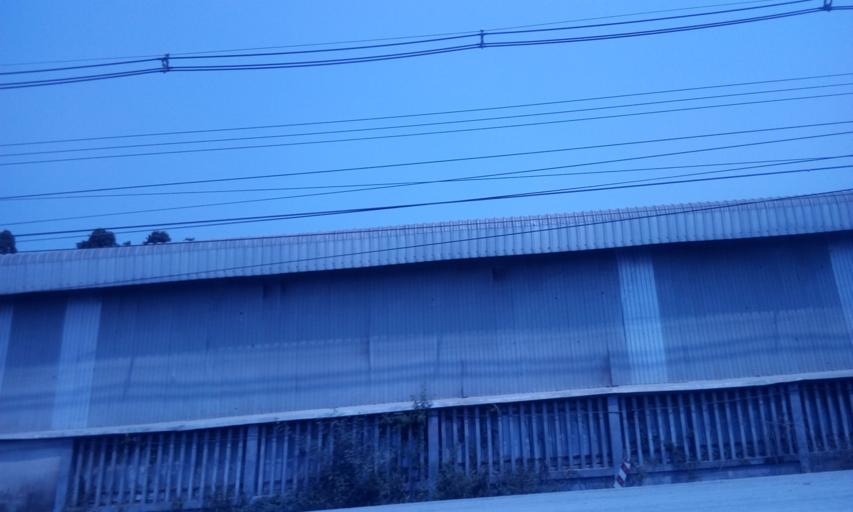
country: TH
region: Chon Buri
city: Phan Thong
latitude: 13.5303
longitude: 101.1508
